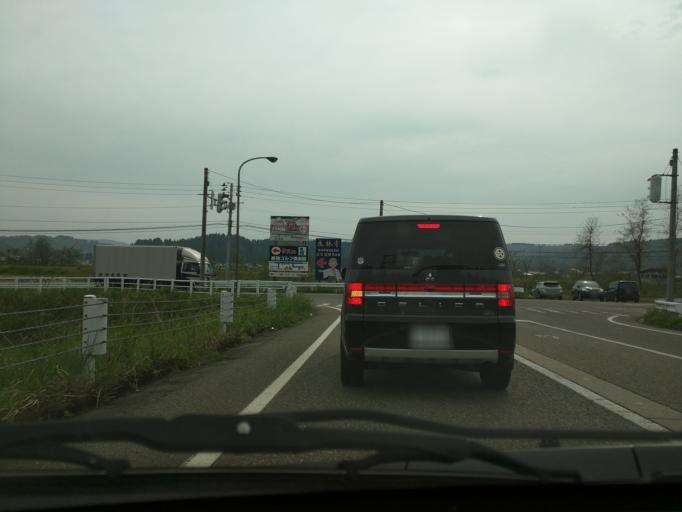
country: JP
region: Niigata
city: Ojiya
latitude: 37.2554
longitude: 138.9206
